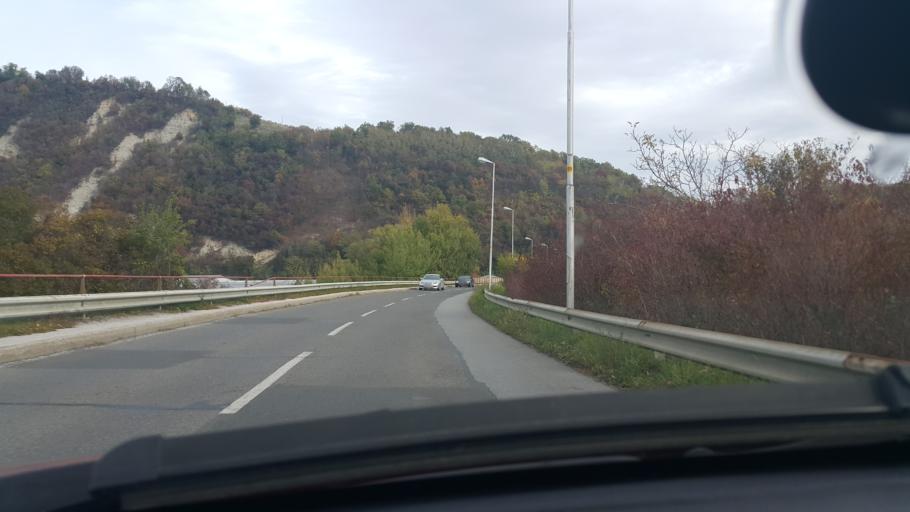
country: SI
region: Maribor
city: Maribor
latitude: 46.5563
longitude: 15.6772
